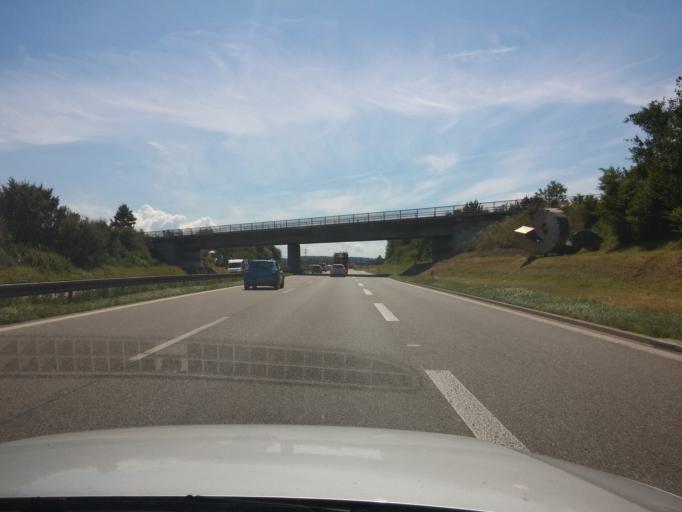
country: DE
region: Baden-Wuerttemberg
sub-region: Tuebingen Region
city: Leutkirch im Allgau
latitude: 47.8369
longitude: 9.9910
